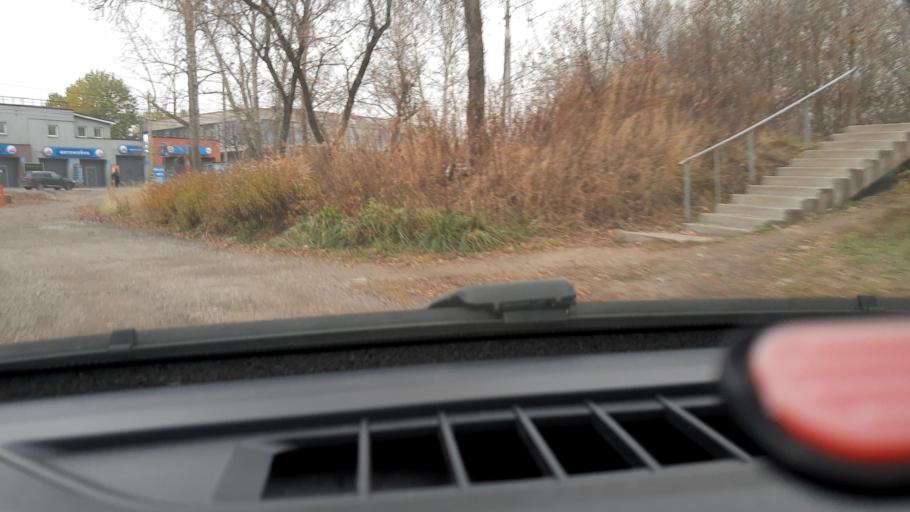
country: RU
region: Nizjnij Novgorod
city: Neklyudovo
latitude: 56.3671
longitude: 43.8474
